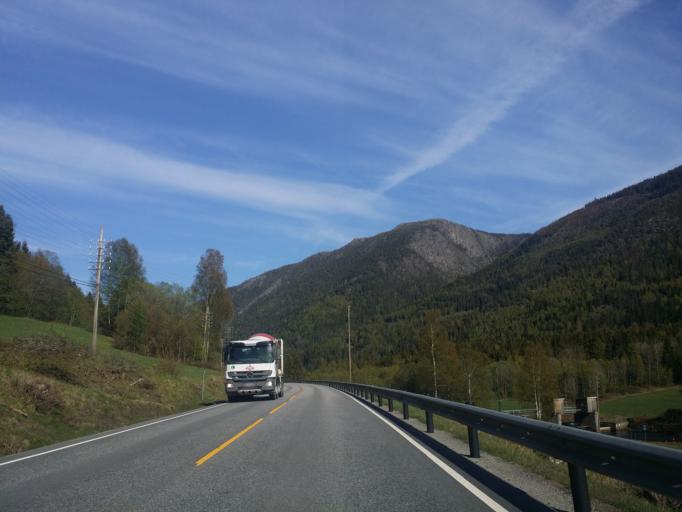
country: NO
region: Telemark
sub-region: Hjartdal
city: Sauland
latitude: 59.6091
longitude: 8.7614
